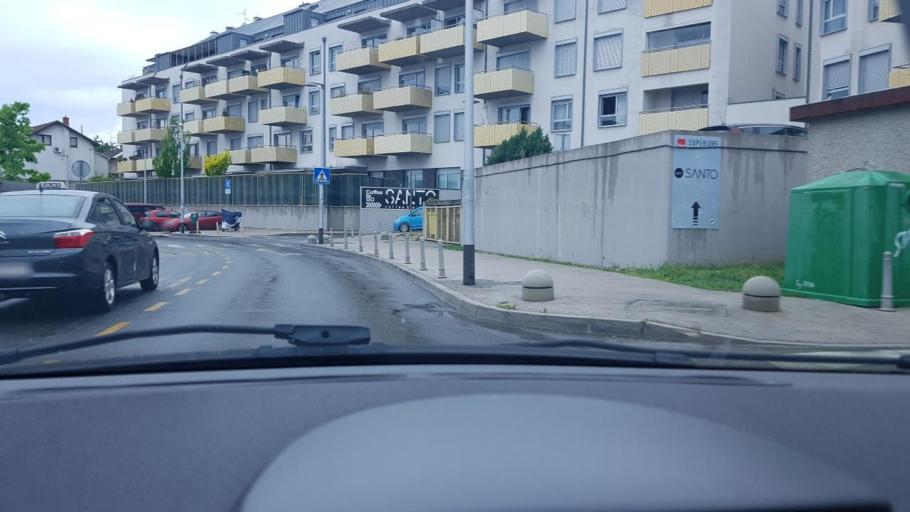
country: HR
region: Grad Zagreb
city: Zagreb - Centar
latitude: 45.8211
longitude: 15.9401
